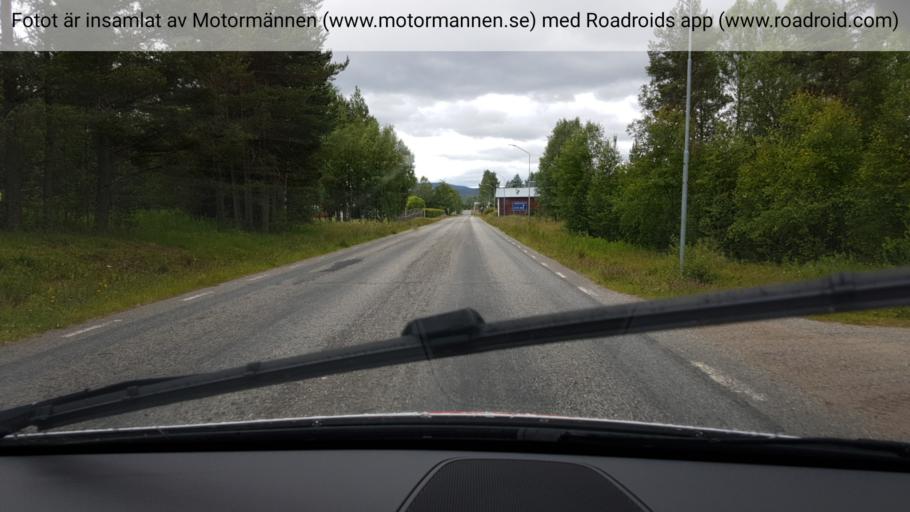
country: SE
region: Jaemtland
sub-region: Harjedalens Kommun
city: Sveg
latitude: 62.3135
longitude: 14.0433
